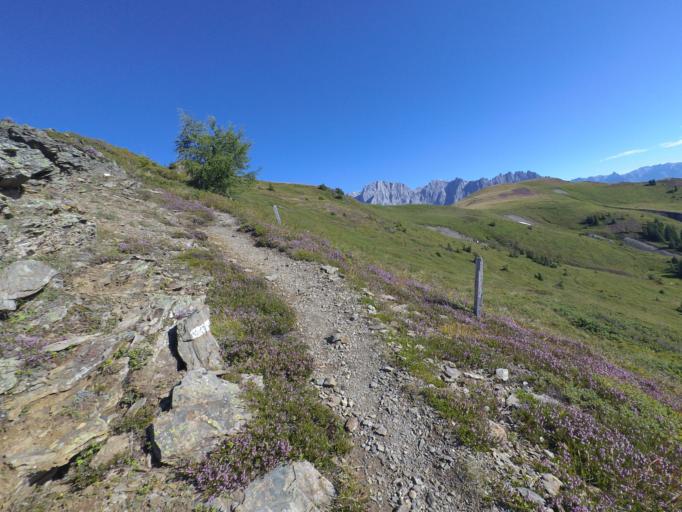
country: AT
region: Salzburg
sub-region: Politischer Bezirk Sankt Johann im Pongau
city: Goldegg
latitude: 47.3642
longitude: 13.0703
